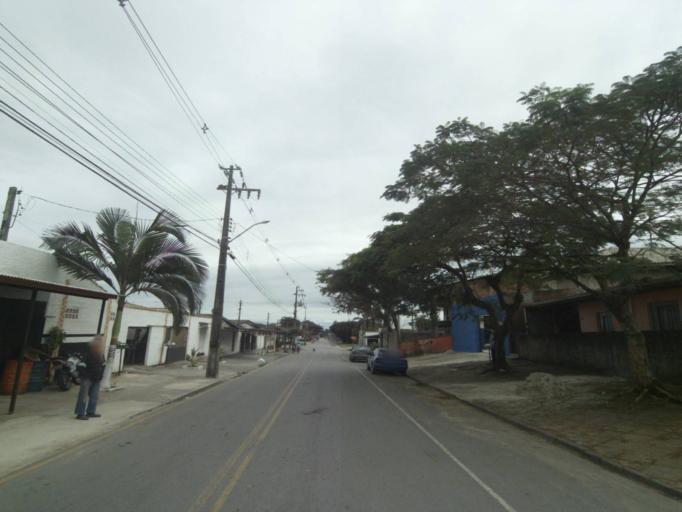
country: BR
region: Parana
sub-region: Paranagua
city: Paranagua
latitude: -25.5163
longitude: -48.5331
